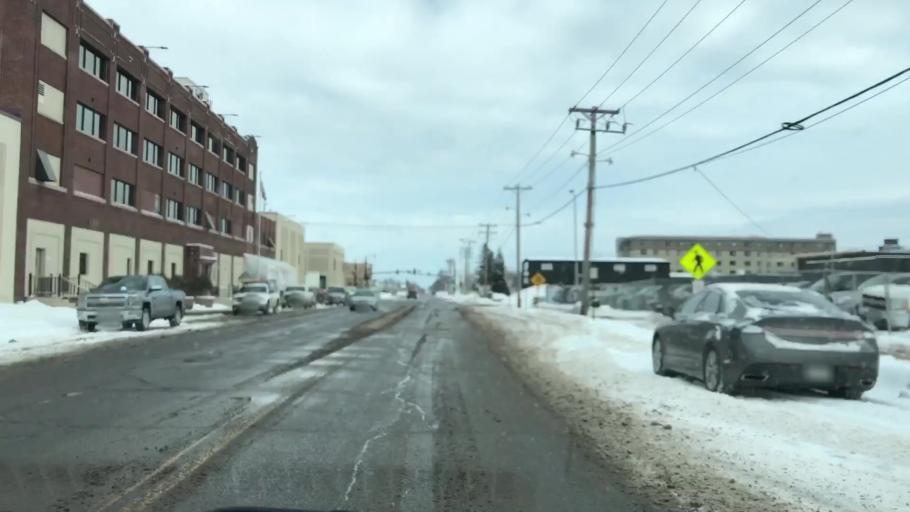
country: US
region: Wisconsin
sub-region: Douglas County
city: Superior
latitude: 46.7279
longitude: -92.1066
